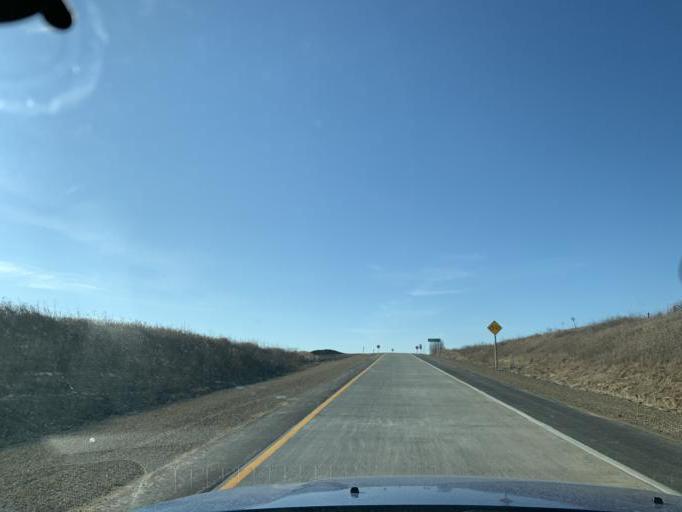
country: US
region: Wisconsin
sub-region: Iowa County
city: Dodgeville
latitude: 42.9380
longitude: -90.1296
